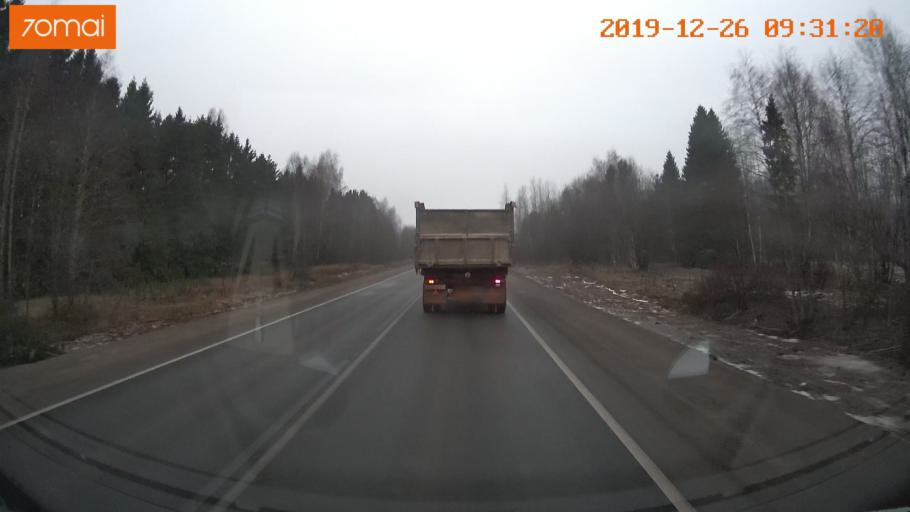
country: RU
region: Vologda
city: Gryazovets
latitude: 59.0682
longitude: 40.1291
